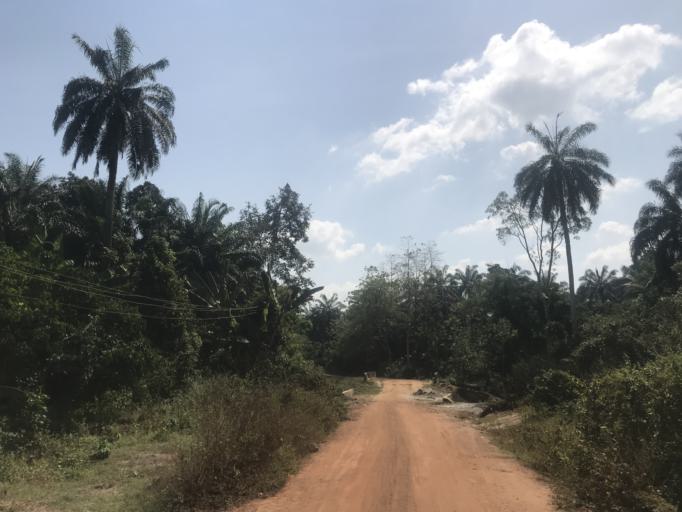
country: NG
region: Osun
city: Iragbiji
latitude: 7.8795
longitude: 4.6996
